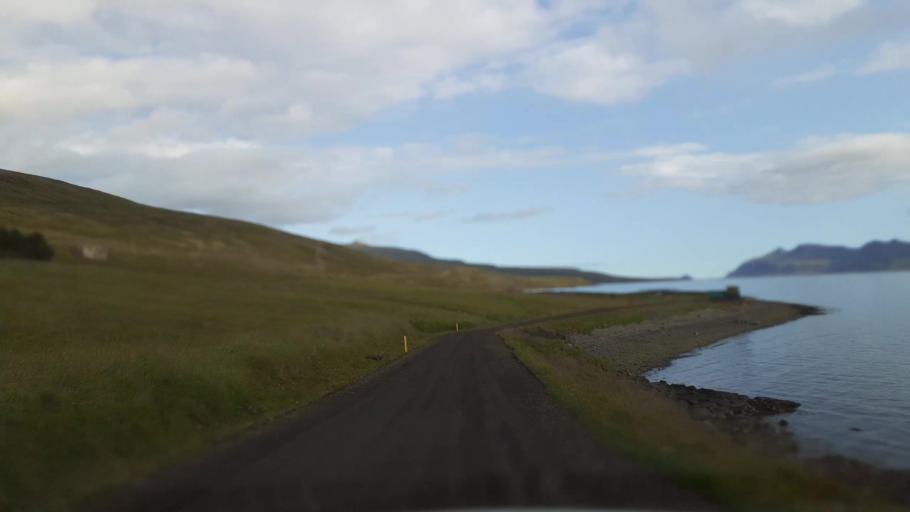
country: IS
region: East
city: Eskifjoerdur
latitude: 65.0378
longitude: -13.8779
